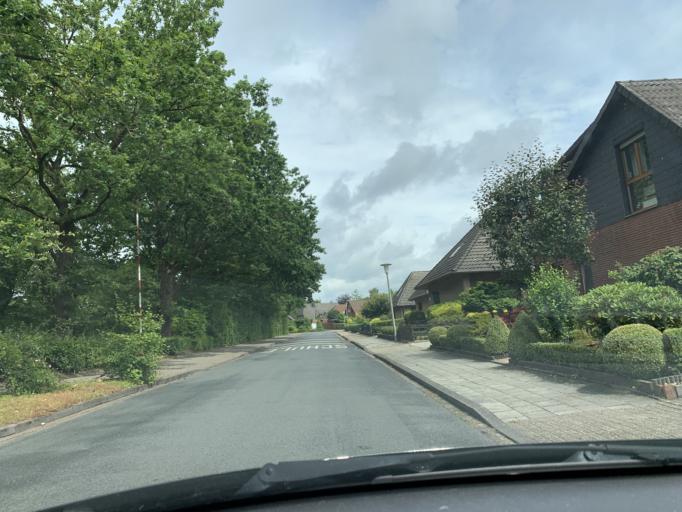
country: DE
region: Lower Saxony
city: Westerstede
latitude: 53.2544
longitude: 7.9379
